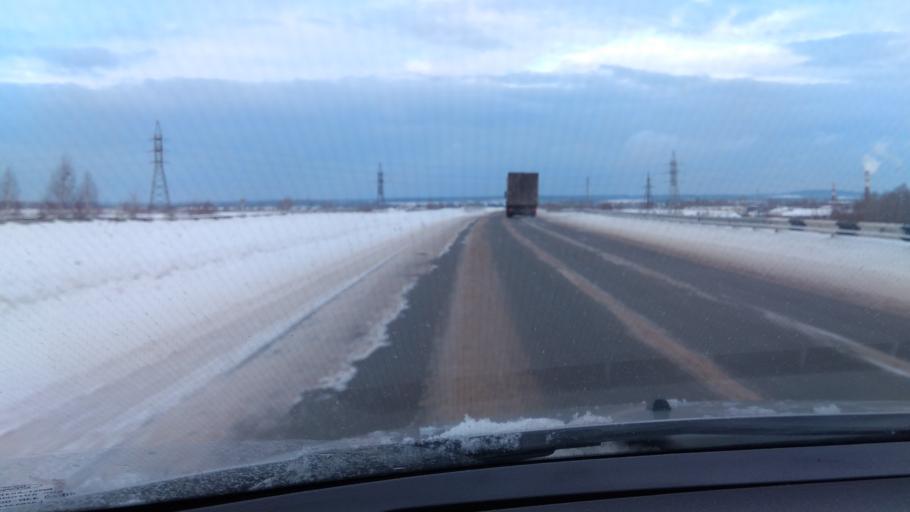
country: RU
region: Sverdlovsk
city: Tsementnyy
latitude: 57.4769
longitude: 60.1804
